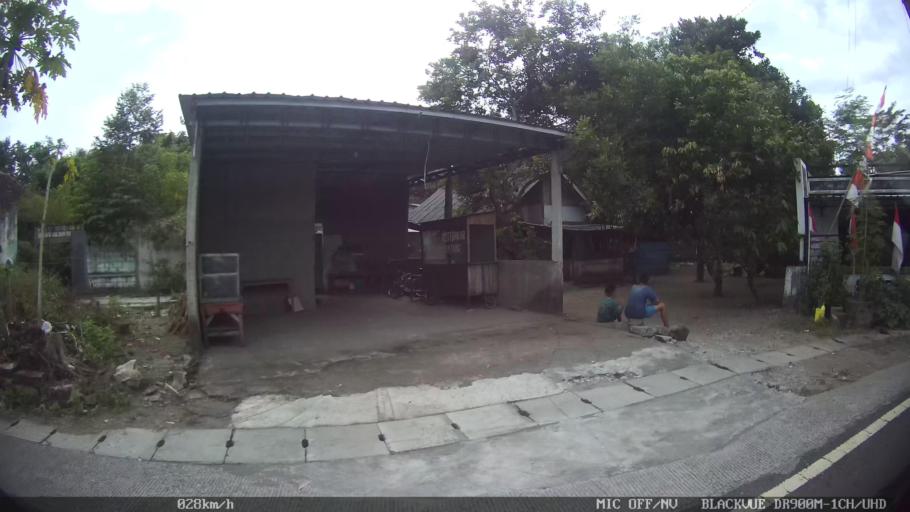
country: ID
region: Daerah Istimewa Yogyakarta
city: Depok
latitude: -7.8065
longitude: 110.4553
